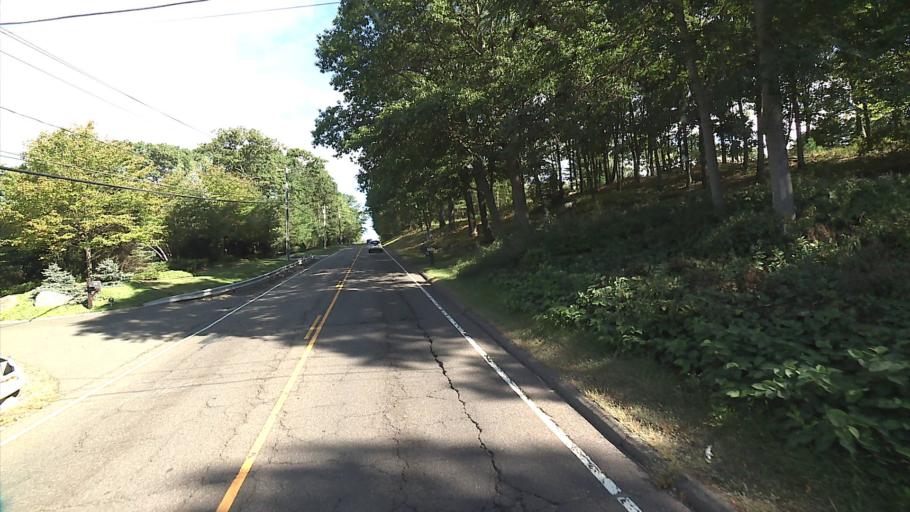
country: US
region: Connecticut
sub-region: Hartford County
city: Bristol
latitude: 41.6394
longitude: -72.9640
